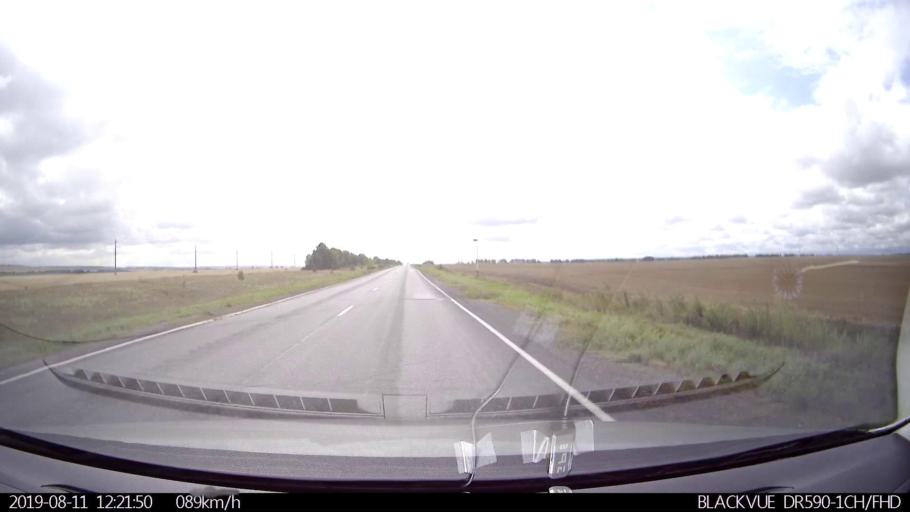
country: RU
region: Ulyanovsk
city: Ignatovka
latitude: 53.9161
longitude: 47.9563
